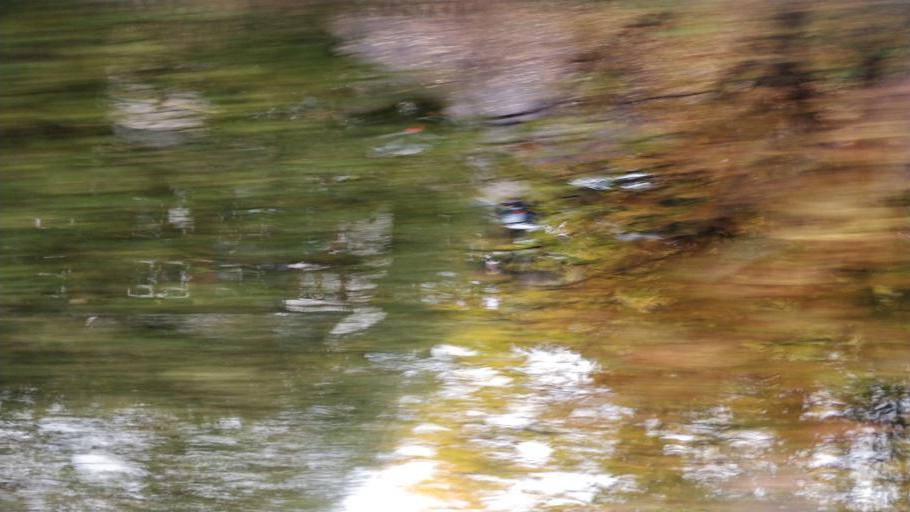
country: GB
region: England
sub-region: Borough of Wigan
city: Ince-in-Makerfield
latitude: 53.5403
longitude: -2.6230
